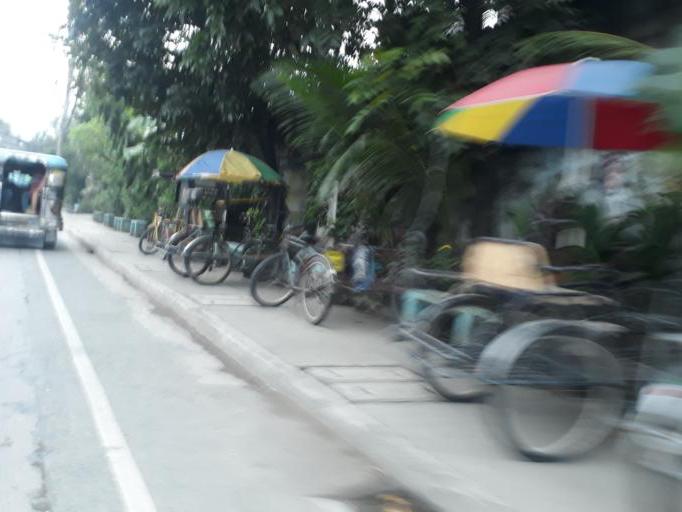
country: PH
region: Calabarzon
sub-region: Province of Rizal
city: Valenzuela
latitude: 14.6959
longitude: 120.9539
